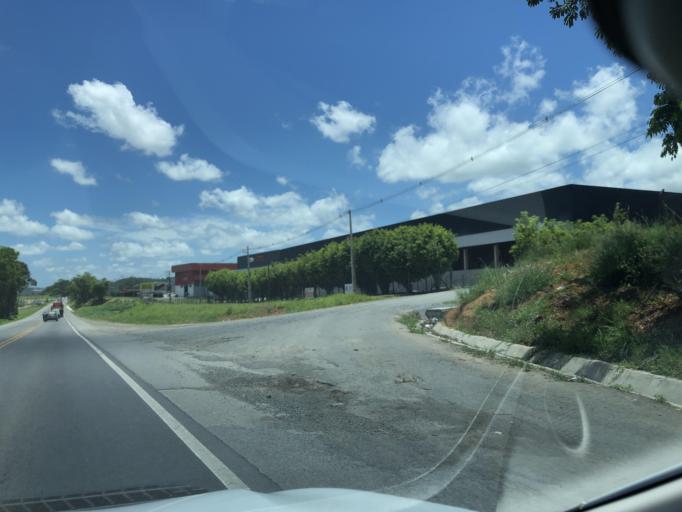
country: BR
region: Santa Catarina
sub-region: Joinville
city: Joinville
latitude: -26.4223
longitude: -48.7818
